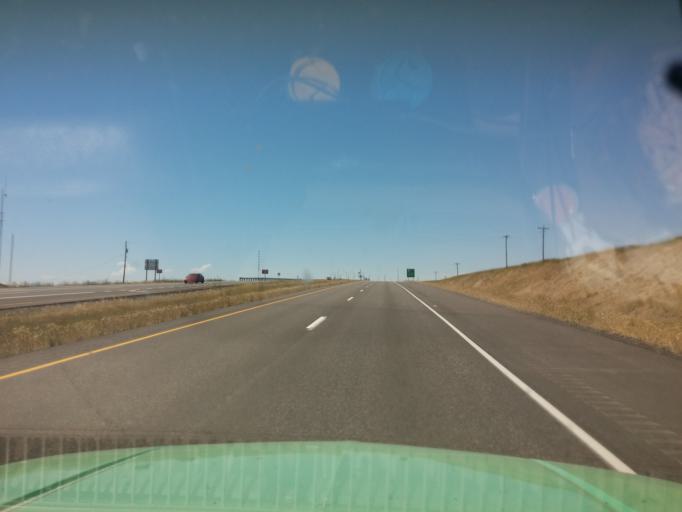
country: US
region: Idaho
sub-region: Nez Perce County
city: Lewiston
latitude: 46.4624
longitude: -117.0051
